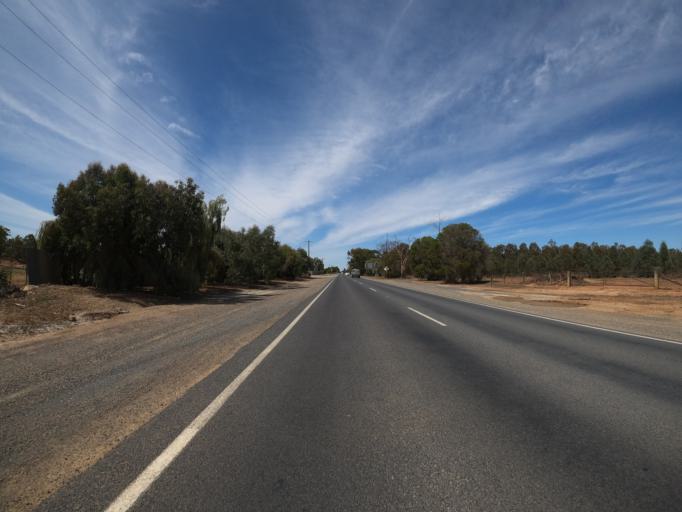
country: AU
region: Victoria
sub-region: Moira
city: Yarrawonga
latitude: -36.0223
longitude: 145.9956
